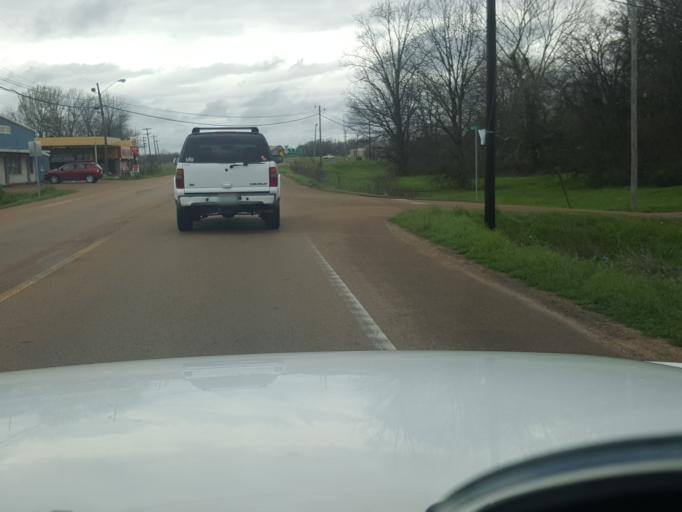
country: US
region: Mississippi
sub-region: Yazoo County
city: Yazoo City
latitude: 32.8515
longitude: -90.4238
